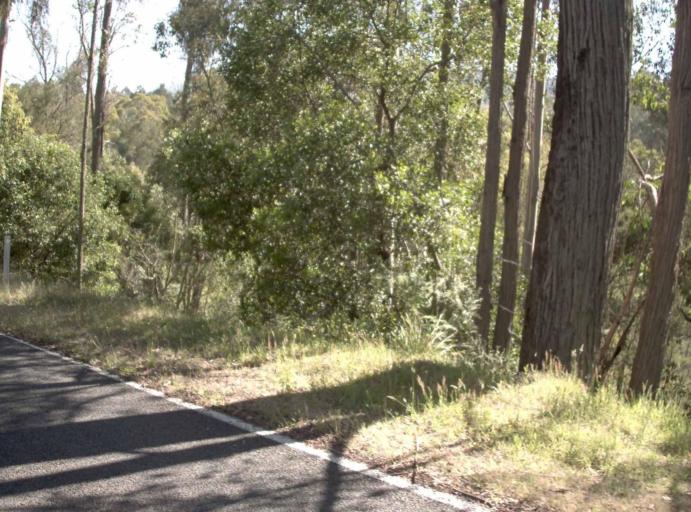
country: AU
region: New South Wales
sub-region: Bombala
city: Bombala
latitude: -37.3426
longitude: 148.6992
